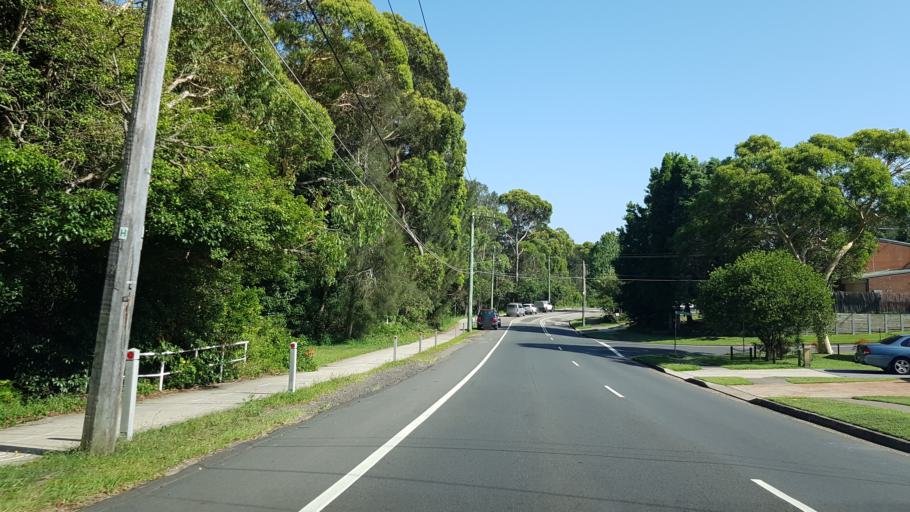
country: AU
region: New South Wales
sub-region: Warringah
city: Narraweena
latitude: -33.7314
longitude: 151.2771
